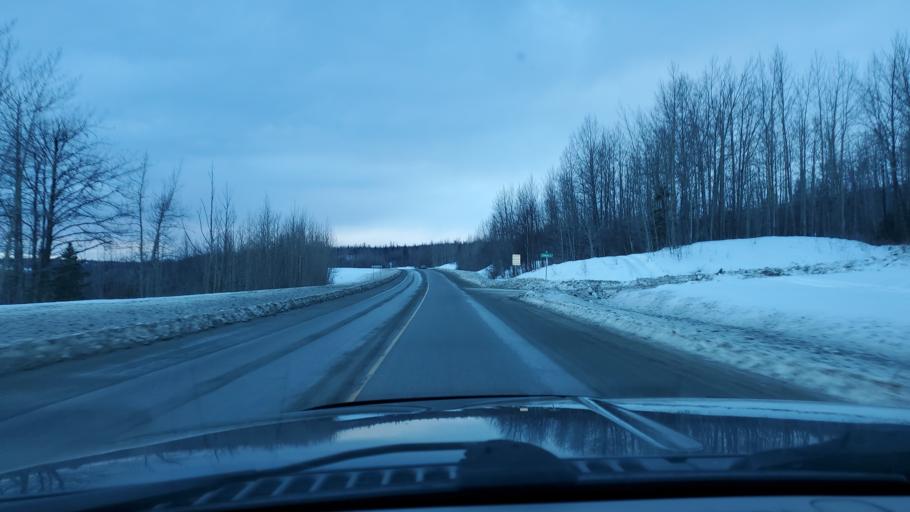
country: US
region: Alaska
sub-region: Matanuska-Susitna Borough
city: Lazy Mountain
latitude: 61.7109
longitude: -148.9054
